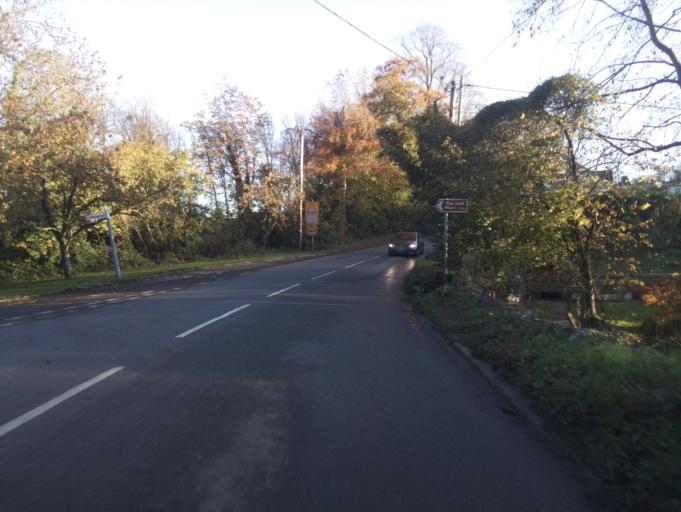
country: GB
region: England
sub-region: Somerset
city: Wincanton
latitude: 51.0118
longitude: -2.4296
